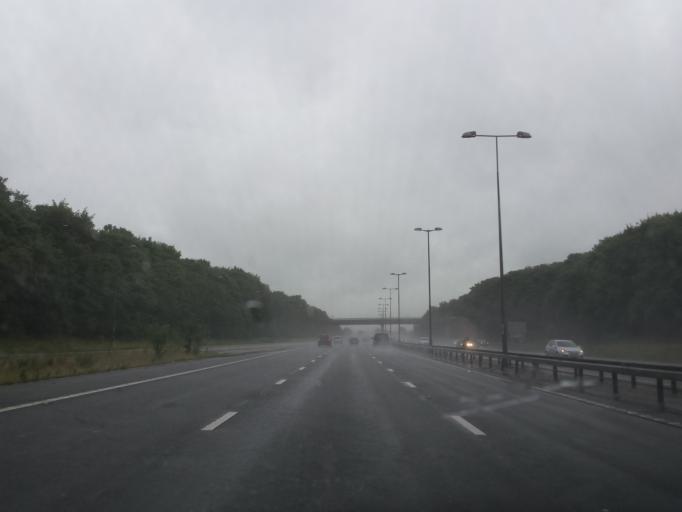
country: GB
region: England
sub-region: Derbyshire
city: Long Eaton
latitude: 52.9130
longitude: -1.2997
